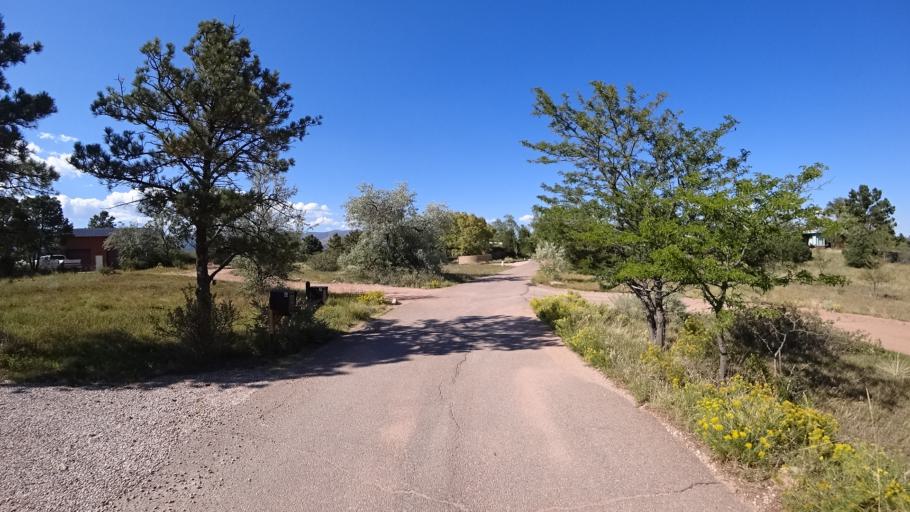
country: US
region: Colorado
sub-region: El Paso County
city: Colorado Springs
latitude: 38.8521
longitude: -104.8445
